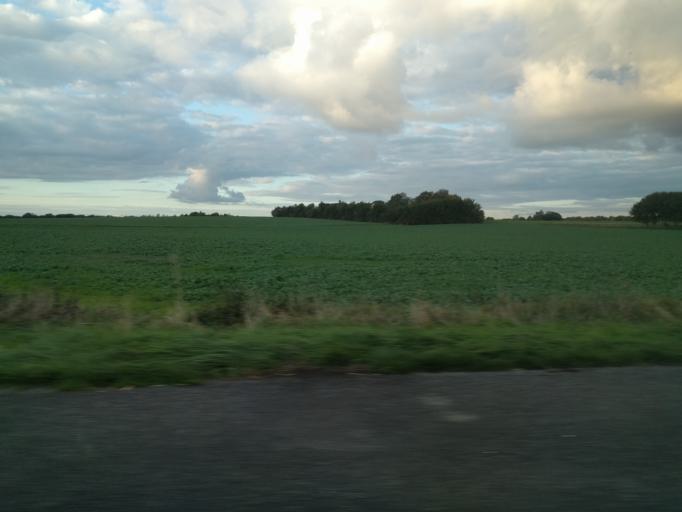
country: DK
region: Zealand
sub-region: Slagelse Kommune
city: Forlev
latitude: 55.3726
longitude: 11.2645
